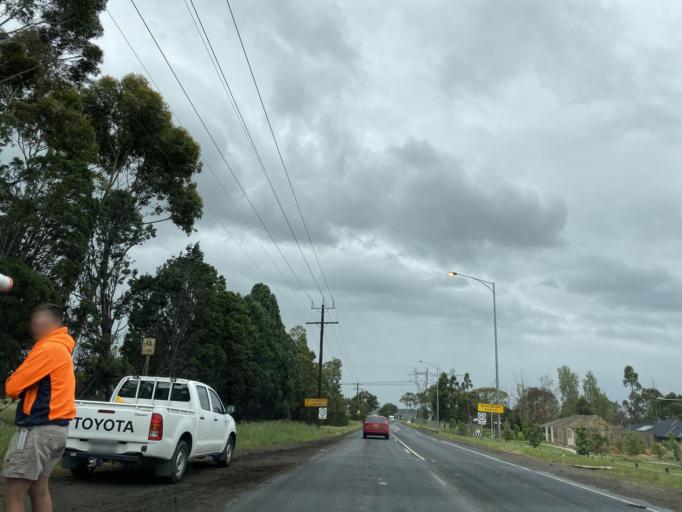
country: AU
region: Victoria
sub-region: Whittlesea
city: Epping
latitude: -37.6065
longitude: 145.0118
